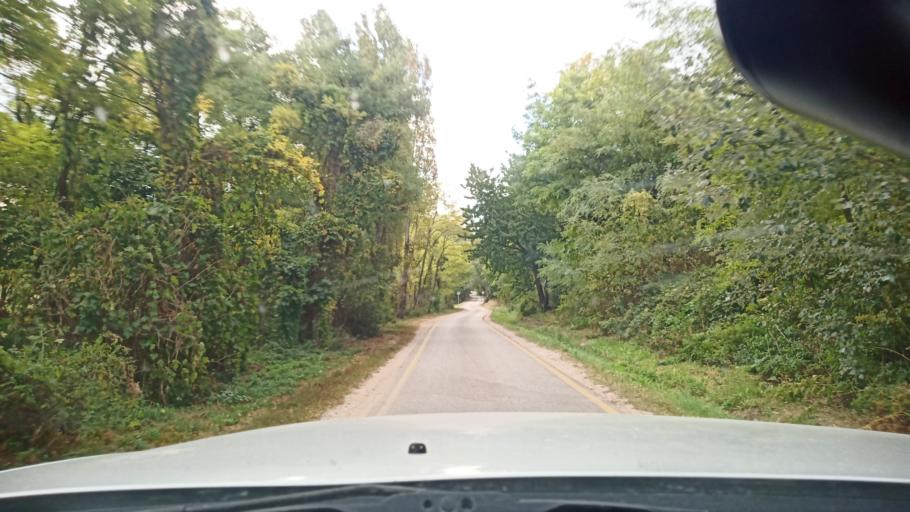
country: HU
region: Fejer
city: Mor
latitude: 47.3748
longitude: 18.2291
